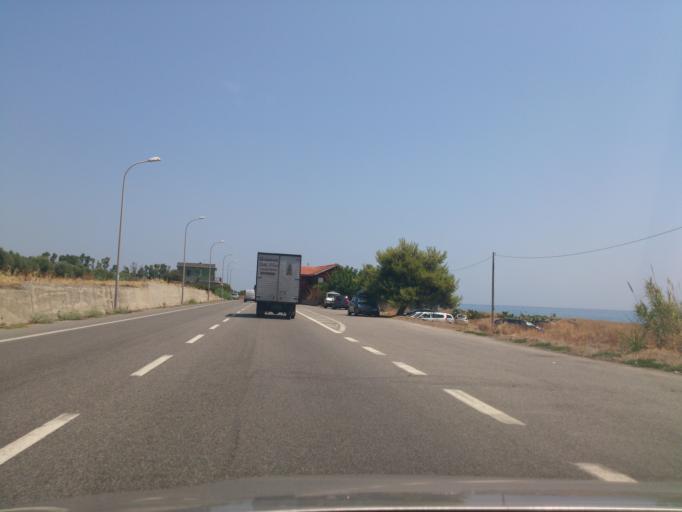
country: IT
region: Calabria
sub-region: Provincia di Reggio Calabria
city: Riace Marina
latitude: 38.4079
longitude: 16.5504
